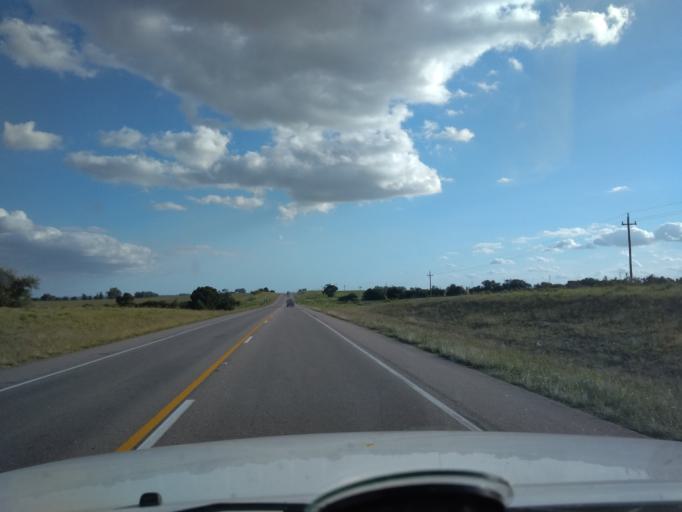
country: UY
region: Florida
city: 25 de Mayo
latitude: -34.3007
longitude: -56.2290
